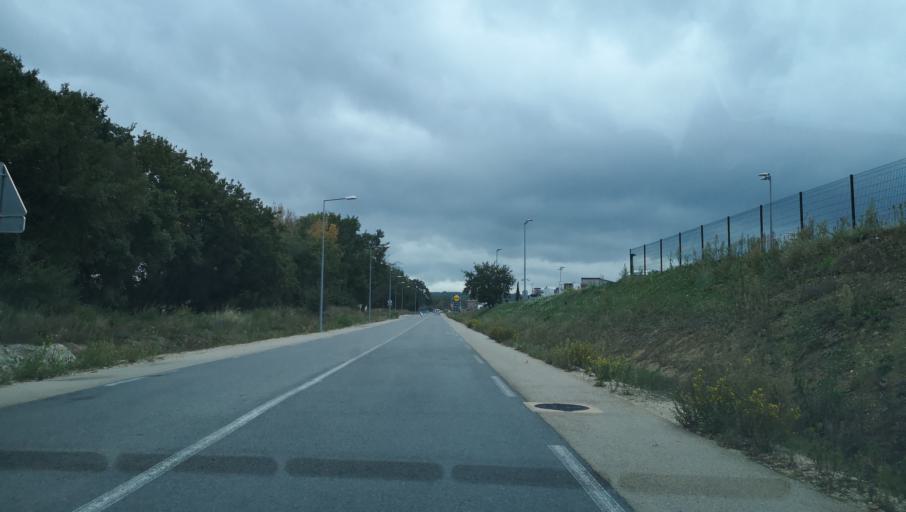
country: FR
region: Provence-Alpes-Cote d'Azur
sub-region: Departement des Bouches-du-Rhone
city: Rousset
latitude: 43.4750
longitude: 5.5936
